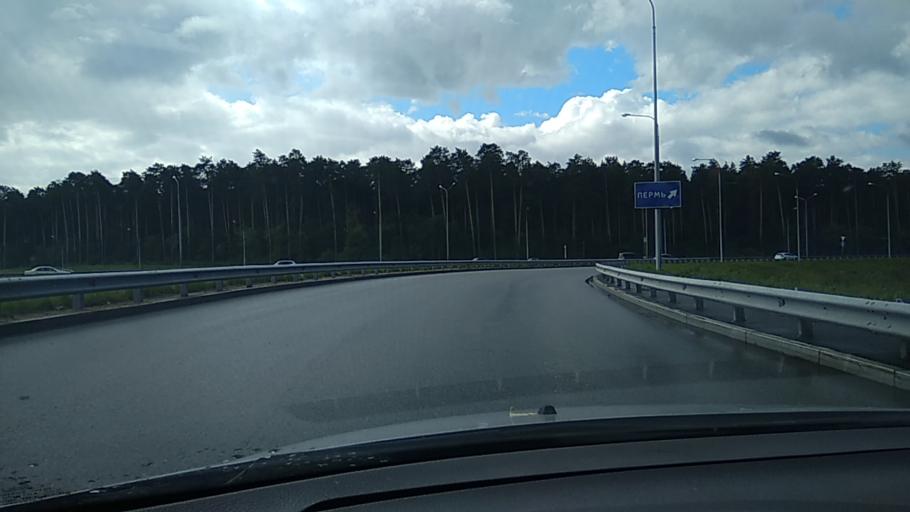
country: RU
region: Sverdlovsk
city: Sovkhoznyy
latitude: 56.7905
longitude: 60.5942
